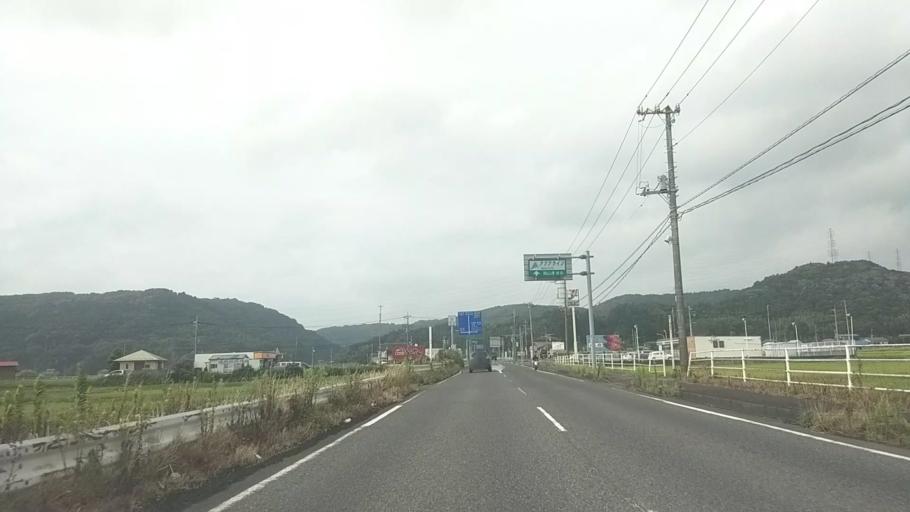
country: JP
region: Chiba
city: Kisarazu
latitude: 35.3009
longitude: 139.9869
